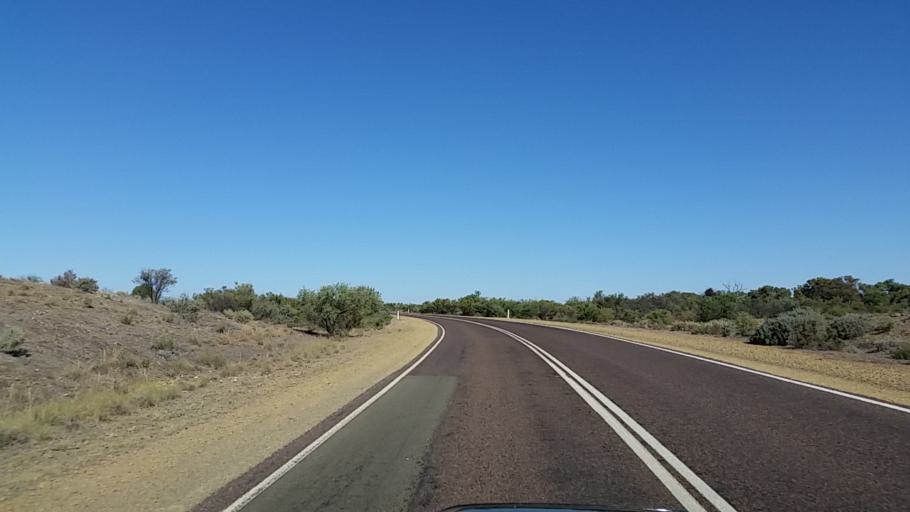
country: AU
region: South Australia
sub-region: Flinders Ranges
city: Quorn
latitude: -32.3349
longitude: 138.4746
